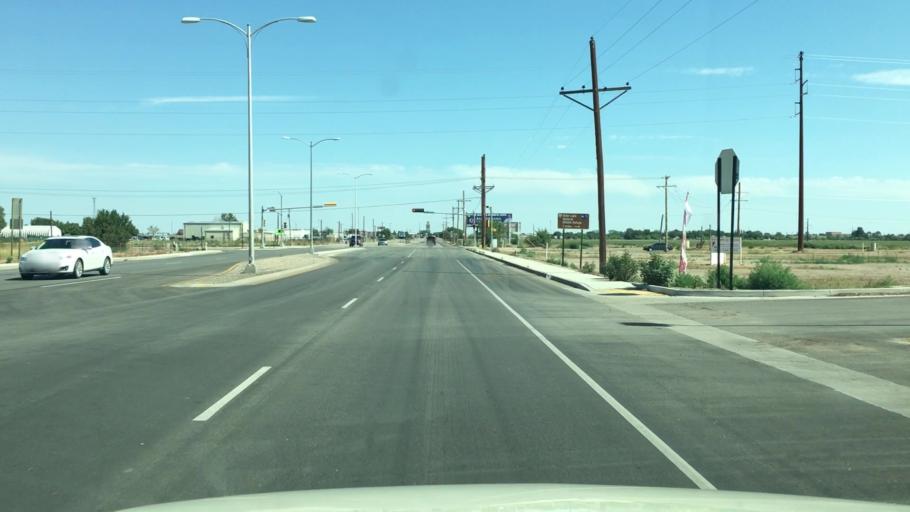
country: US
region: New Mexico
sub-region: Chaves County
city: Roswell
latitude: 33.4510
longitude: -104.5233
